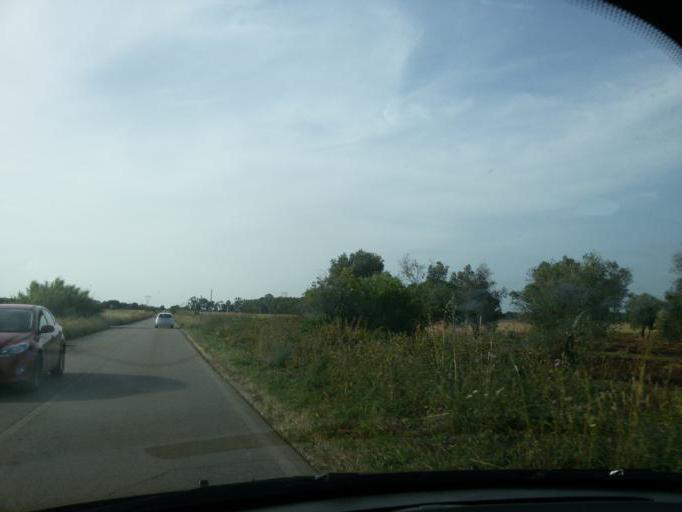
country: IT
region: Apulia
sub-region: Provincia di Lecce
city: Porto Cesareo
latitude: 40.3316
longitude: 17.8520
